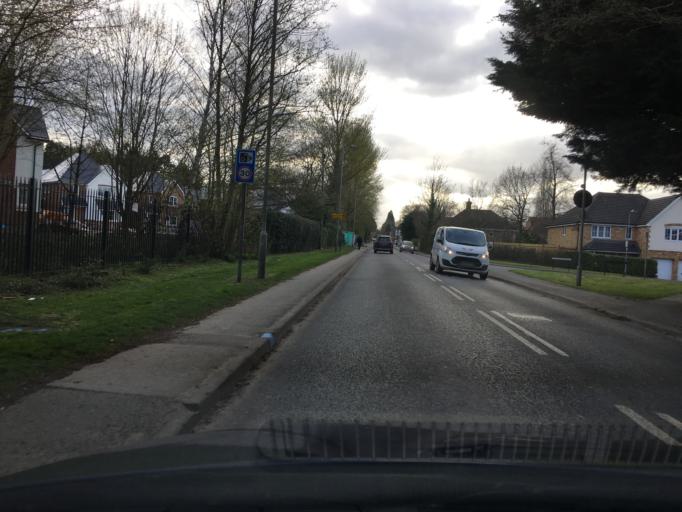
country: GB
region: England
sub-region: Bracknell Forest
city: Crowthorne
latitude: 51.3680
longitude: -0.8135
